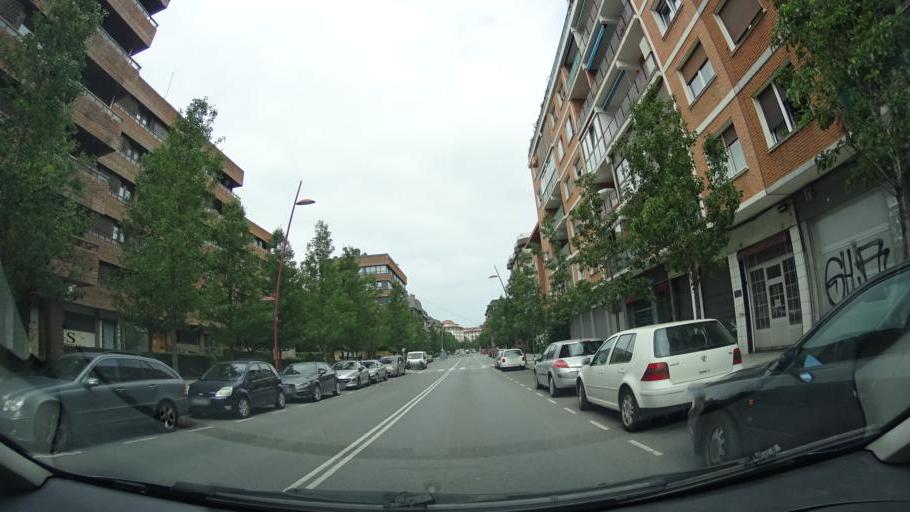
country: ES
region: Basque Country
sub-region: Bizkaia
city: Portugalete
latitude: 43.3212
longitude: -3.0122
